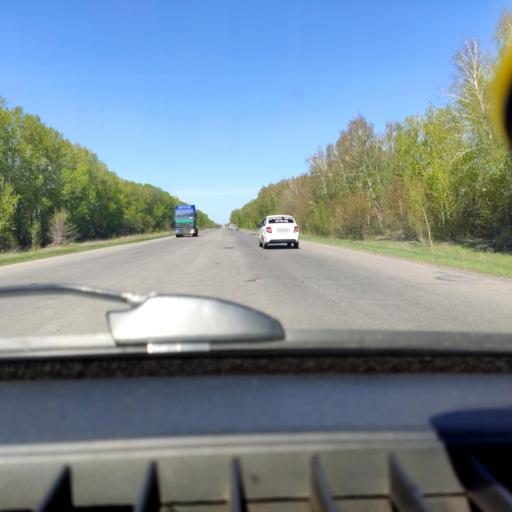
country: RU
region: Samara
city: Tol'yatti
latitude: 53.6408
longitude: 49.4201
